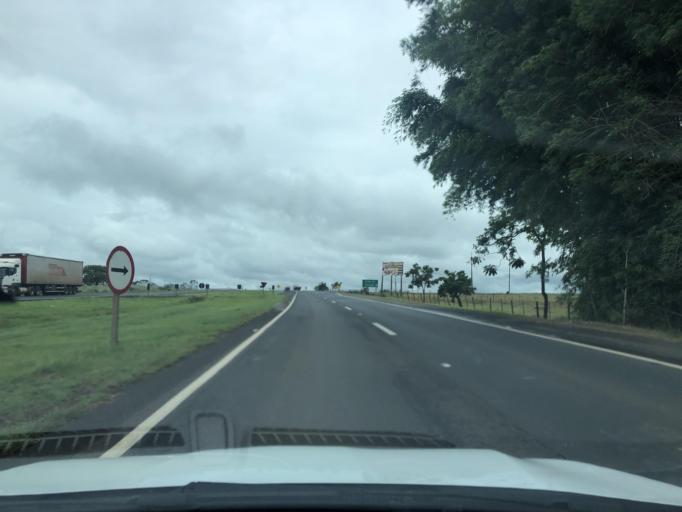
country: BR
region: Minas Gerais
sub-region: Uberaba
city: Uberaba
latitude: -19.6213
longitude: -48.0174
